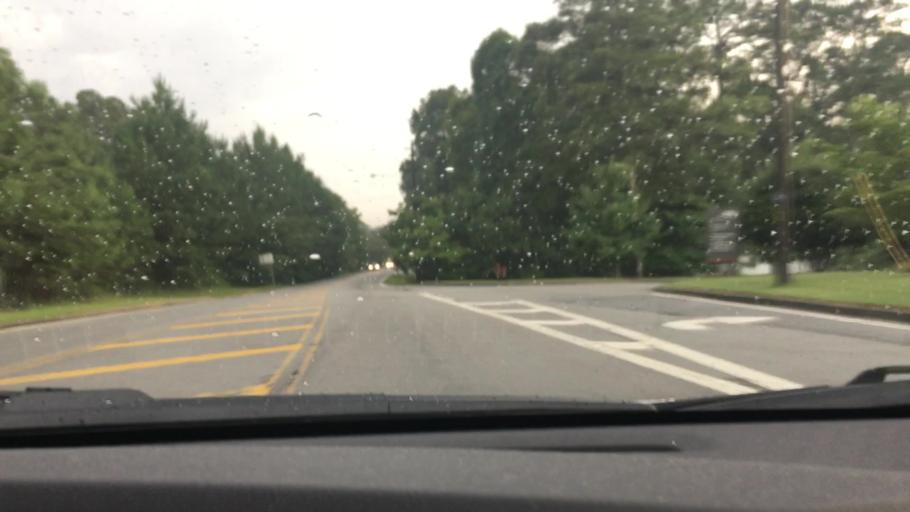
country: US
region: Georgia
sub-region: Fulton County
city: Union City
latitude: 33.6415
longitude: -84.5234
